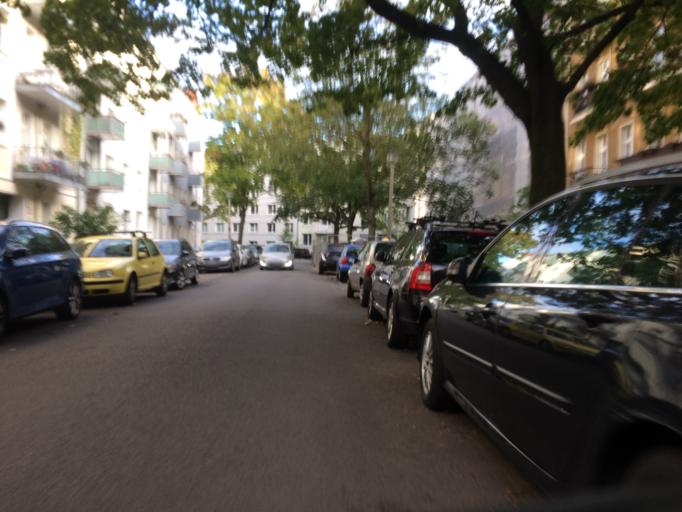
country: DE
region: Berlin
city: Pankow
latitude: 52.5625
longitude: 13.3969
